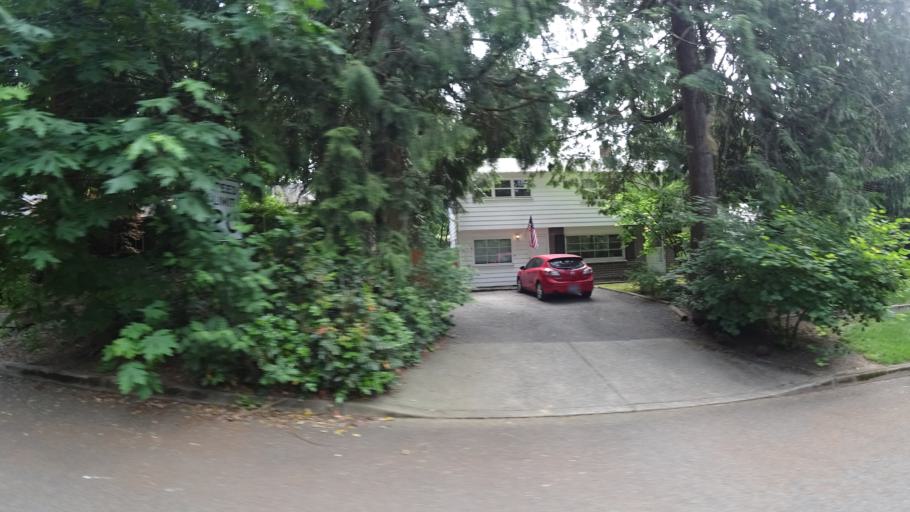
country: US
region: Oregon
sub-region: Washington County
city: Metzger
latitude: 45.4516
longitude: -122.7300
